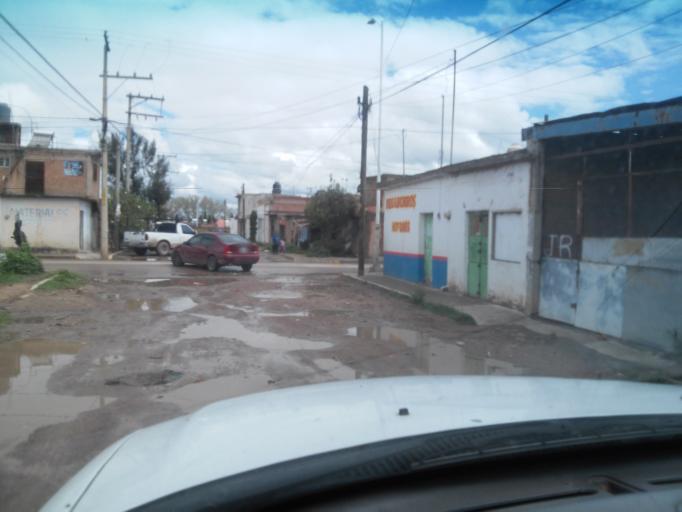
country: MX
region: Durango
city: Victoria de Durango
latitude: 24.0177
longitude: -104.6123
